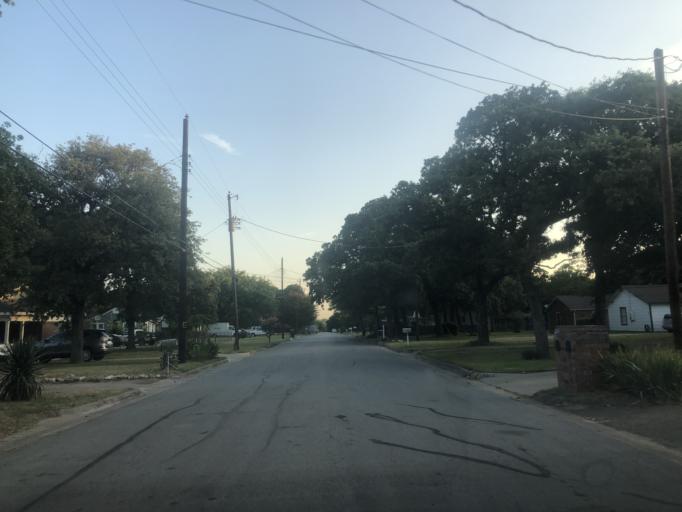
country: US
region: Texas
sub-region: Tarrant County
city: Lake Worth
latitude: 32.8024
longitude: -97.4469
